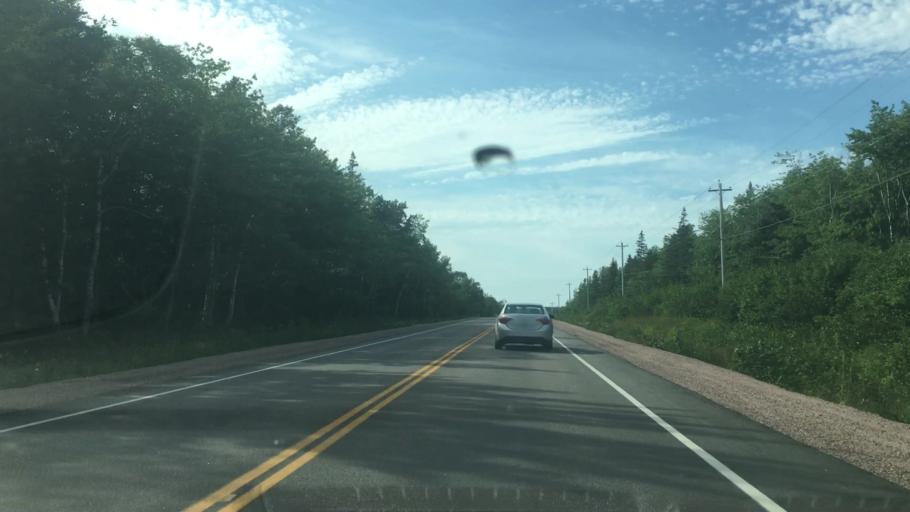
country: CA
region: Nova Scotia
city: Sydney Mines
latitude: 46.8190
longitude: -60.3500
